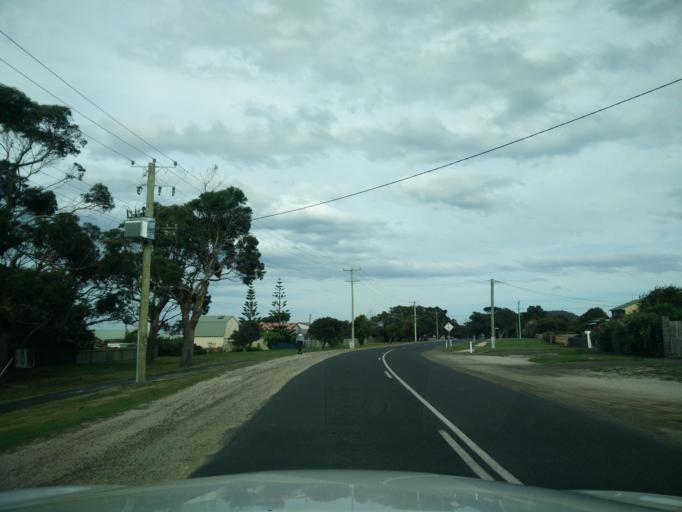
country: AU
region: Tasmania
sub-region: Break O'Day
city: St Helens
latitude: -41.8695
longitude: 148.2904
